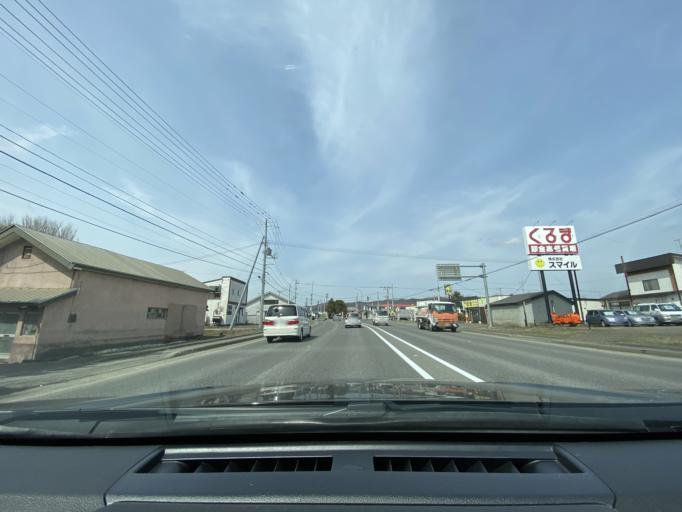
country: JP
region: Hokkaido
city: Kitami
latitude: 43.8032
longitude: 143.8145
